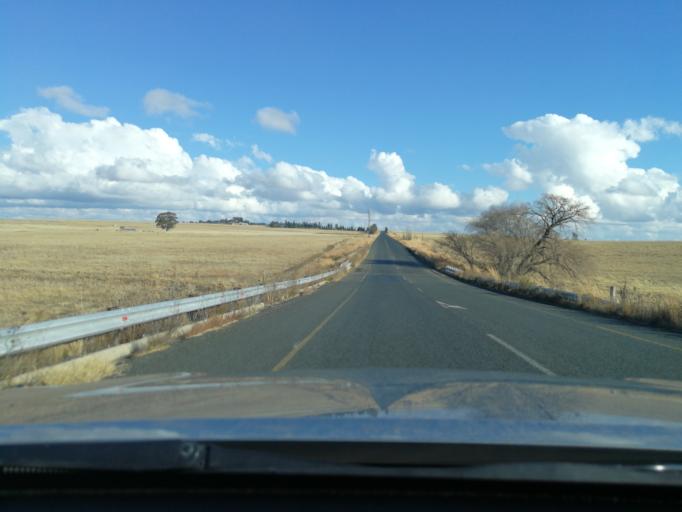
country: ZA
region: Orange Free State
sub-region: Thabo Mofutsanyana District Municipality
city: Bethlehem
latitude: -28.0528
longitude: 28.3655
